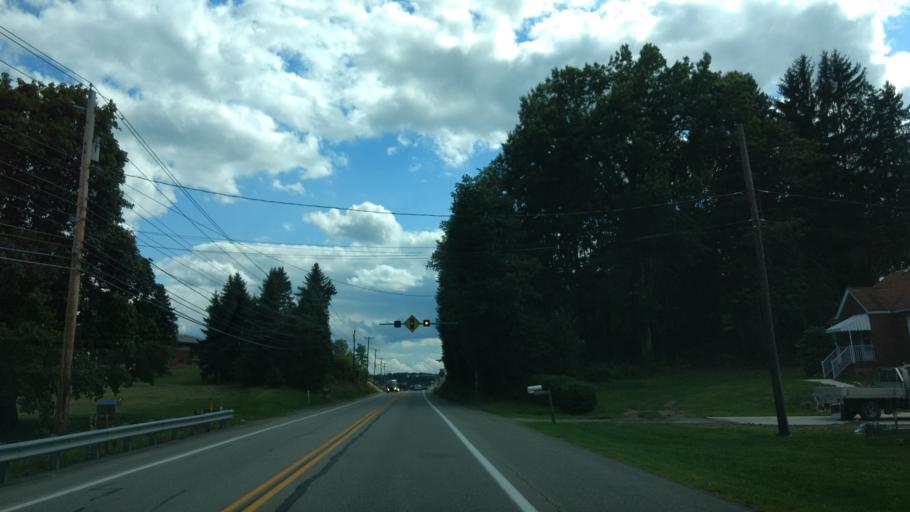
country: US
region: Pennsylvania
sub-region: Armstrong County
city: Apollo
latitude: 40.5348
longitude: -79.5947
